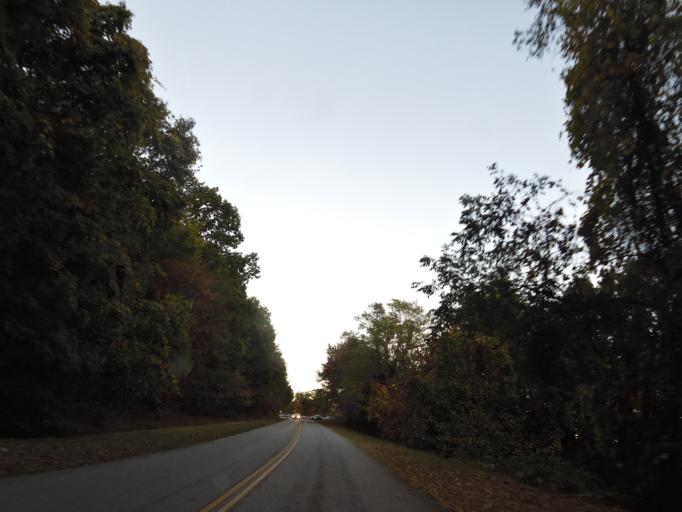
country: US
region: Tennessee
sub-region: Blount County
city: Maryville
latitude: 35.6310
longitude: -83.9431
